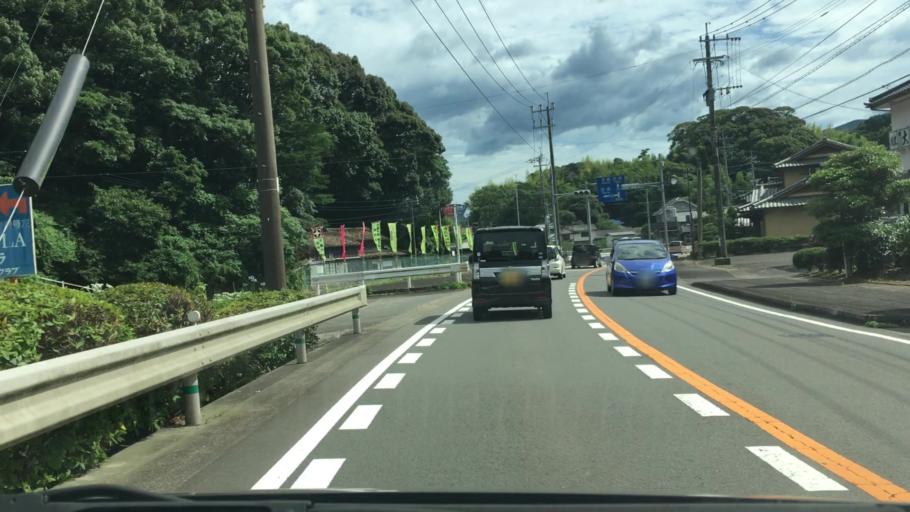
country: JP
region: Nagasaki
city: Togitsu
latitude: 32.9531
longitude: 129.7856
